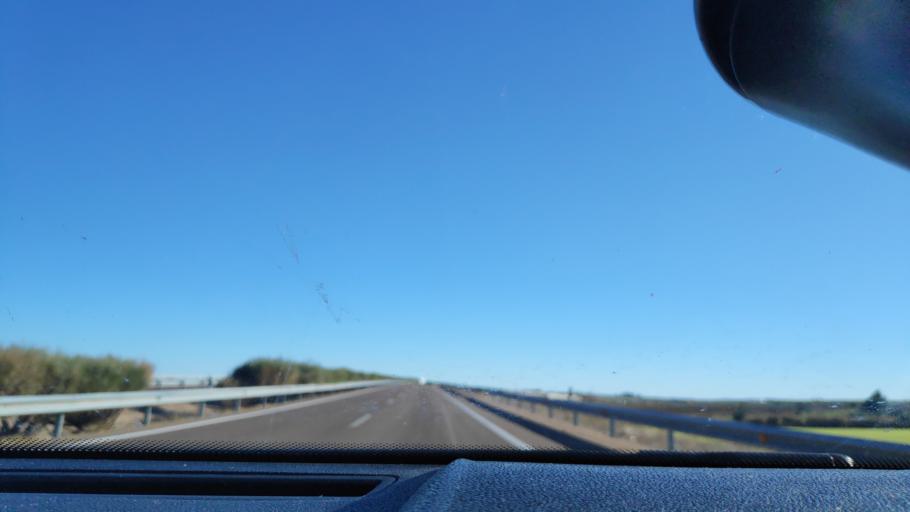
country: ES
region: Extremadura
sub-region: Provincia de Badajoz
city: Villafranca de los Barros
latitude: 38.5326
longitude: -6.3561
